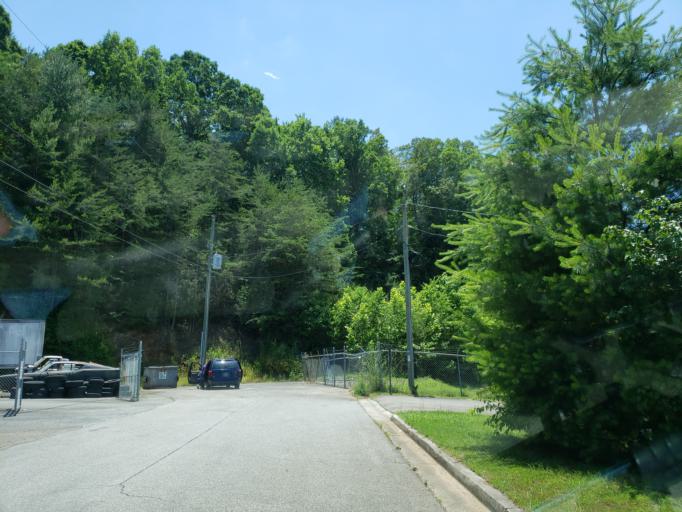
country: US
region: Georgia
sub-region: Gilmer County
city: Ellijay
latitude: 34.6788
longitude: -84.4849
